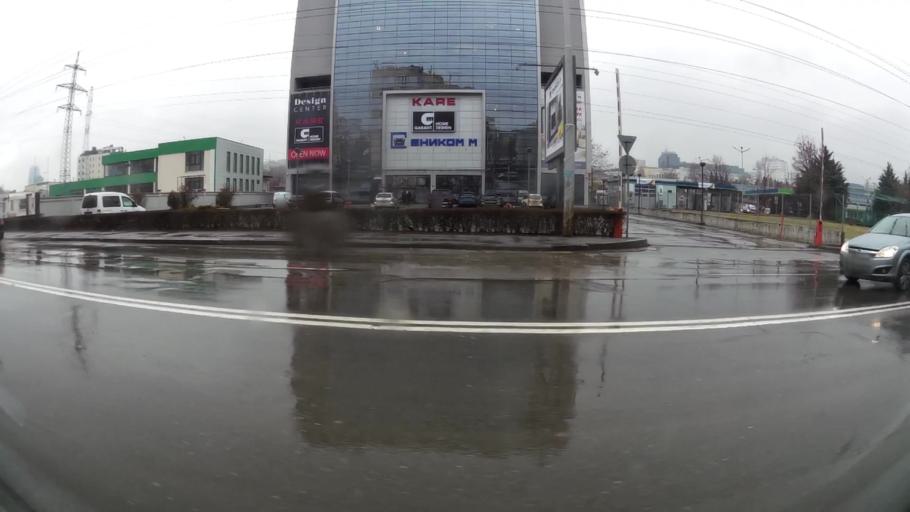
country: BG
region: Sofia-Capital
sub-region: Stolichna Obshtina
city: Sofia
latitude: 42.6616
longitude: 23.3932
